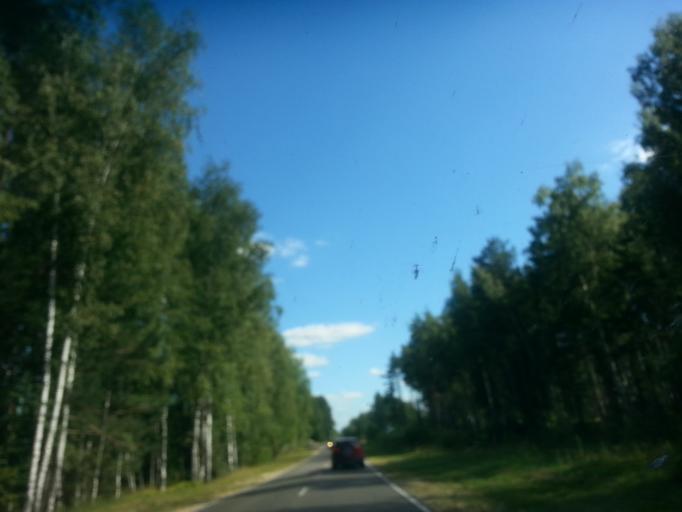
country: RU
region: Nizjnij Novgorod
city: Taremskoye
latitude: 56.0066
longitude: 42.9869
